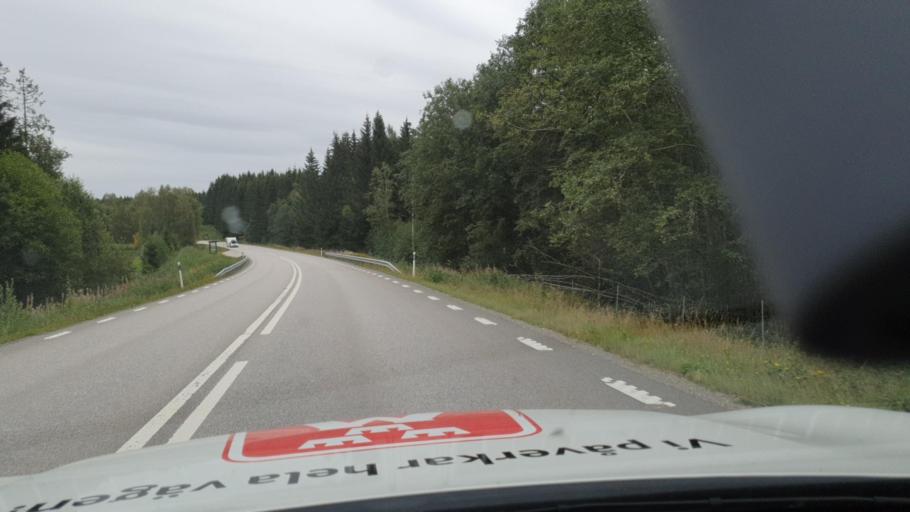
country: SE
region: Vaestra Goetaland
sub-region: Bengtsfors Kommun
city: Billingsfors
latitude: 59.0220
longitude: 12.3681
